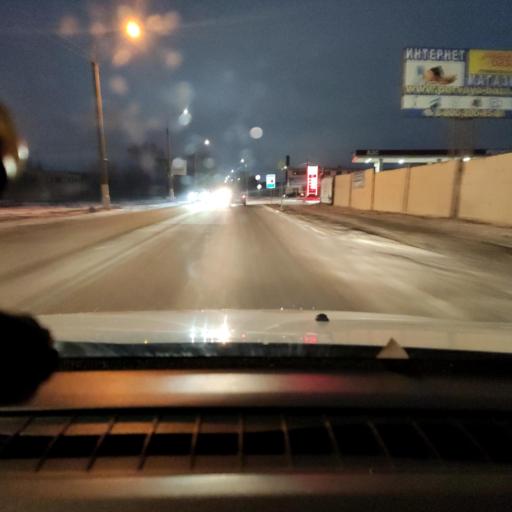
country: RU
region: Samara
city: Chapayevsk
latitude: 52.9650
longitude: 49.6929
